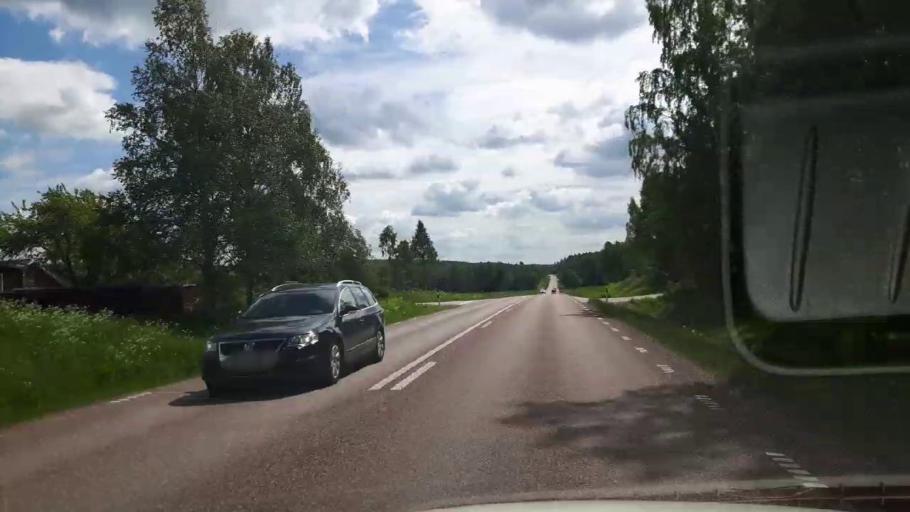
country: SE
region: Dalarna
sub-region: Hedemora Kommun
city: Hedemora
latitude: 60.3776
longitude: 15.9131
